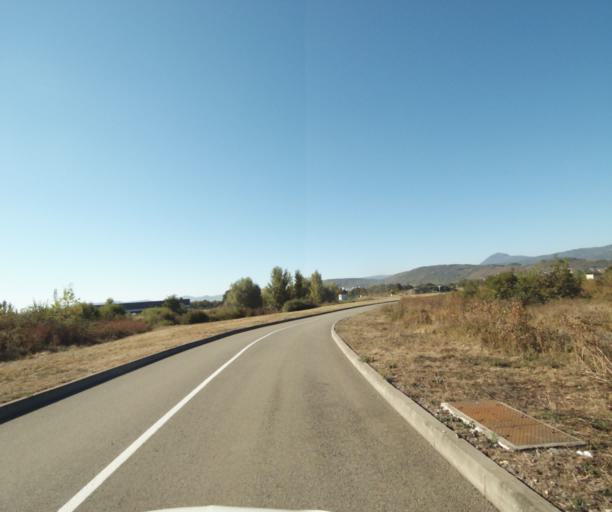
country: FR
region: Auvergne
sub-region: Departement du Puy-de-Dome
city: Gerzat
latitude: 45.8330
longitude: 3.1286
